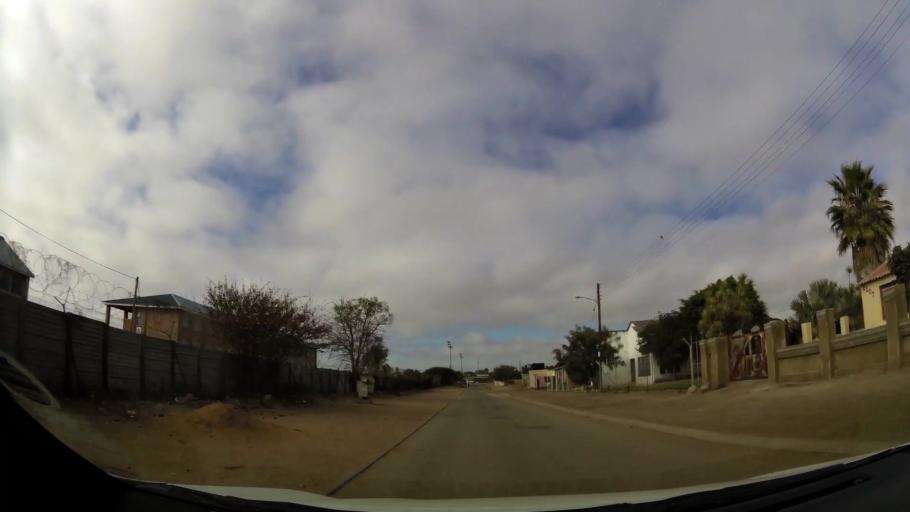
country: ZA
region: Limpopo
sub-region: Capricorn District Municipality
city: Polokwane
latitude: -23.8517
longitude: 29.3871
